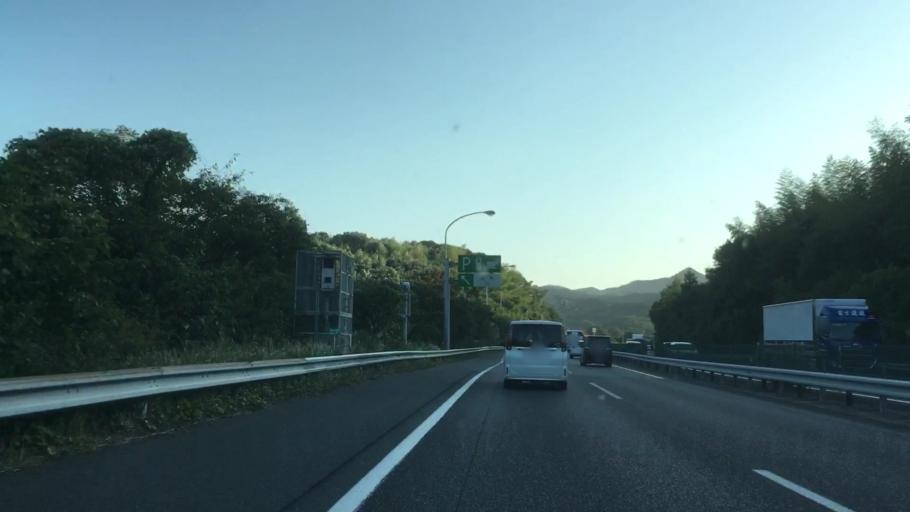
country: JP
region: Yamaguchi
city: Shimonoseki
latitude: 34.0540
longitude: 131.0065
